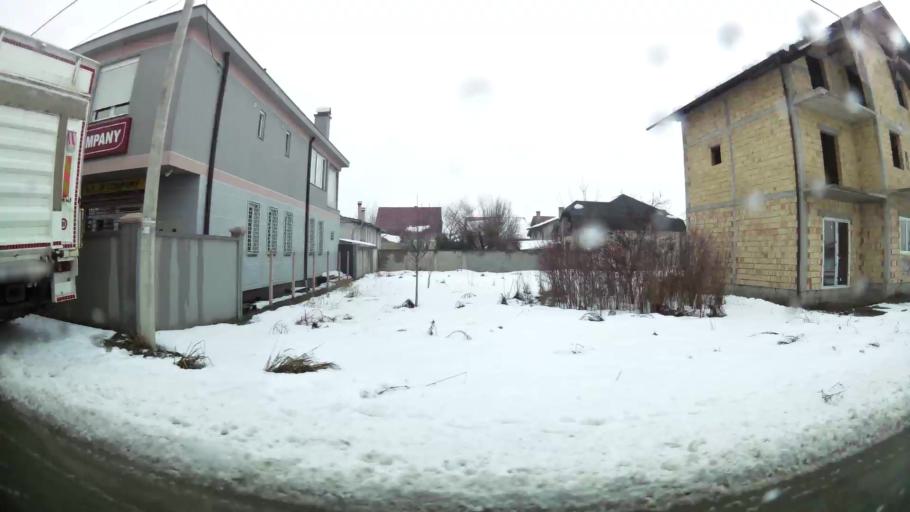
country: RS
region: Central Serbia
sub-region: Belgrade
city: Zemun
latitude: 44.8588
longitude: 20.3441
